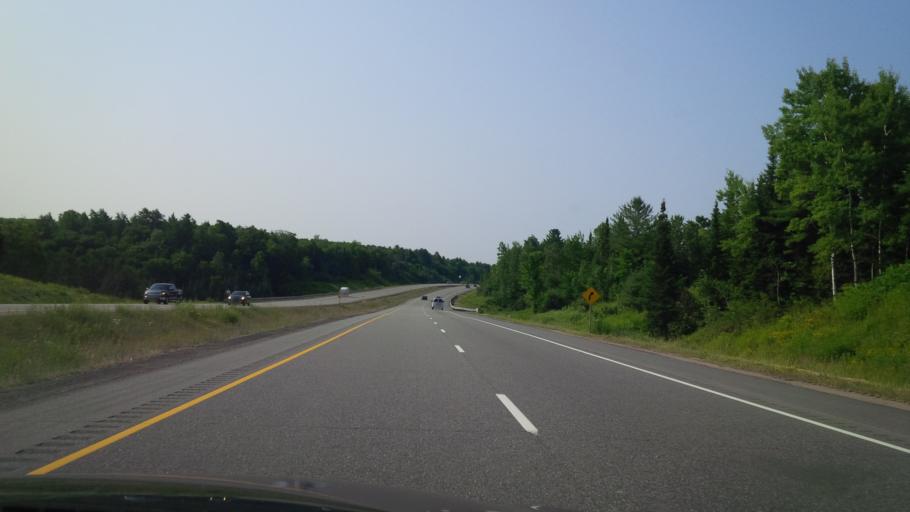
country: CA
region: Ontario
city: Bracebridge
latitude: 45.0304
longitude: -79.2928
